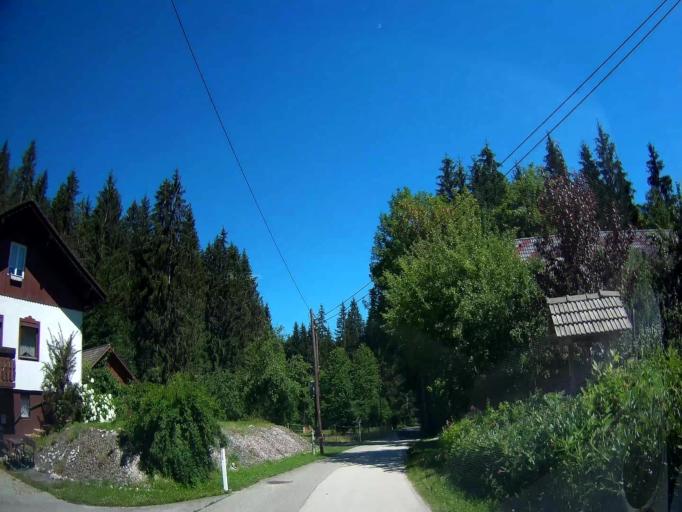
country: AT
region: Carinthia
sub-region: Politischer Bezirk Volkermarkt
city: Gallizien
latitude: 46.5395
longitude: 14.5093
